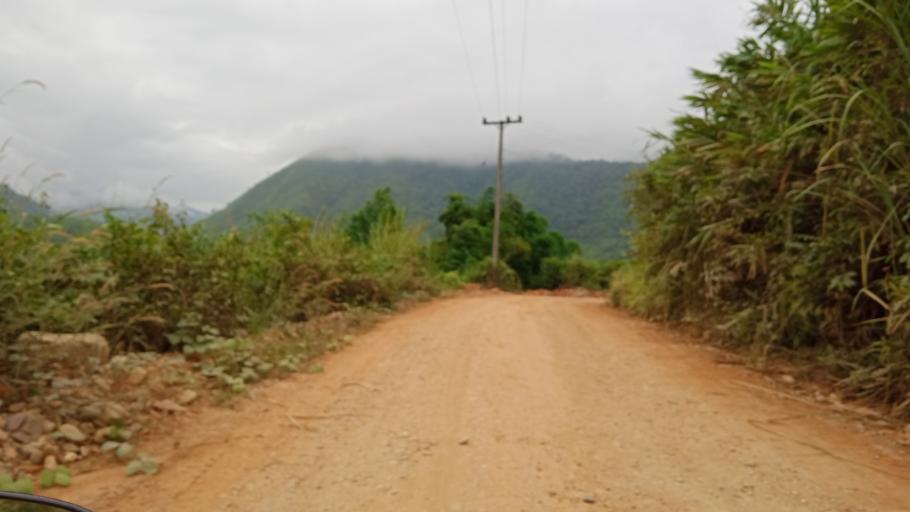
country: LA
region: Xiangkhoang
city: Phonsavan
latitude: 19.0916
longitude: 102.9853
